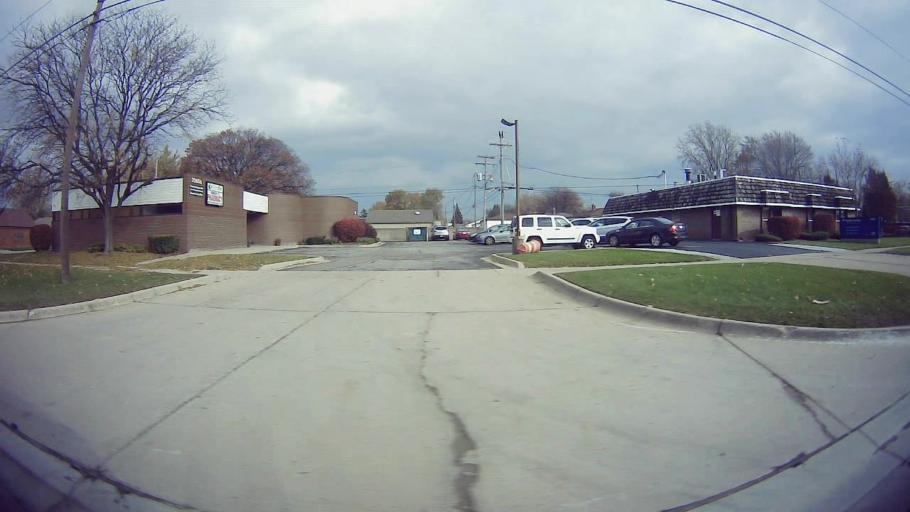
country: US
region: Michigan
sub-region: Macomb County
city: Eastpointe
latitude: 42.4836
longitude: -82.9868
